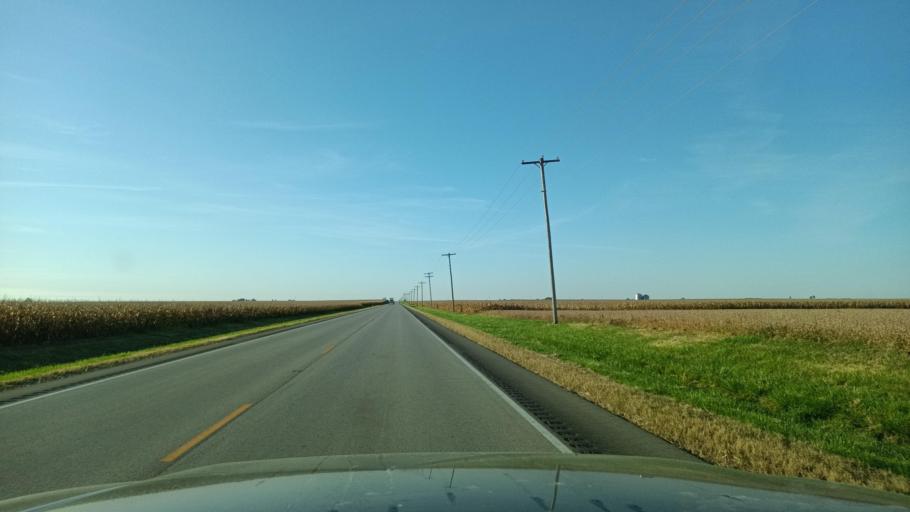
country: US
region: Illinois
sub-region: Douglas County
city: Villa Grove
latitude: 39.7843
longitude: -87.9397
